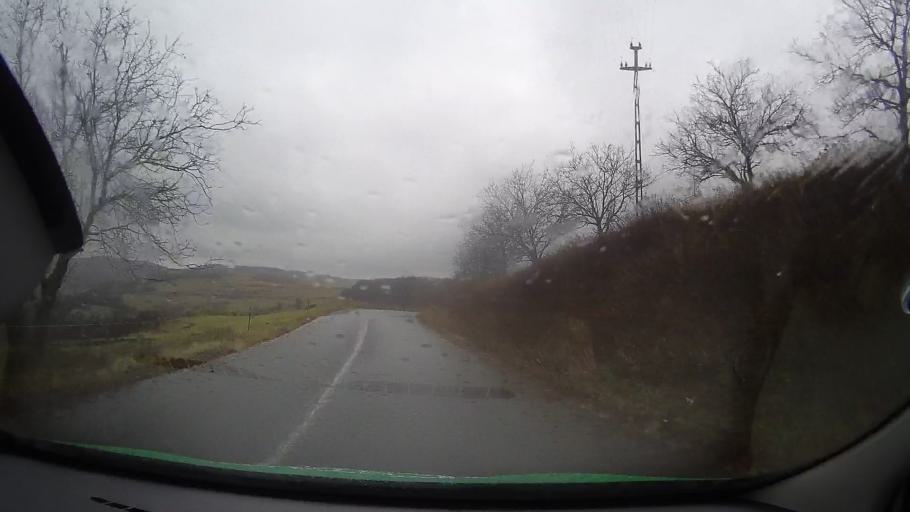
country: RO
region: Mures
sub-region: Comuna Vatava
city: Vatava
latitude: 46.9547
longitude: 24.7450
